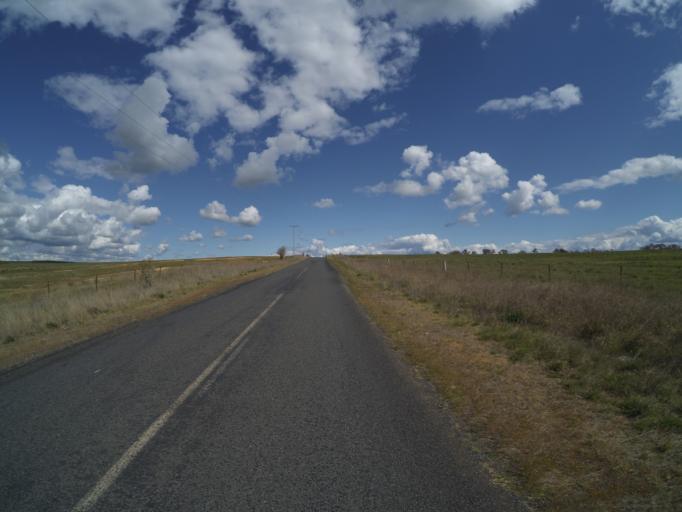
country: AU
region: New South Wales
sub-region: Yass Valley
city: Yass
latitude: -34.8906
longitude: 148.8940
